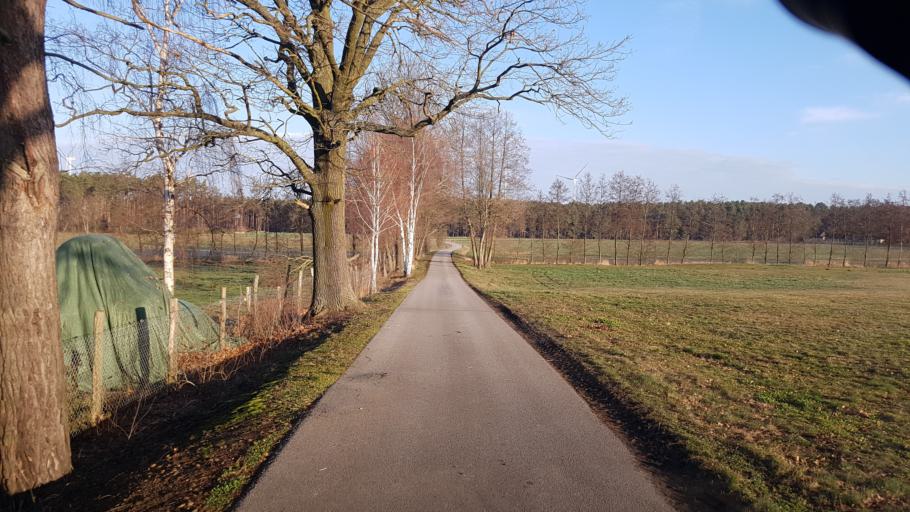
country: DE
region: Brandenburg
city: Calau
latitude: 51.7311
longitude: 13.8990
